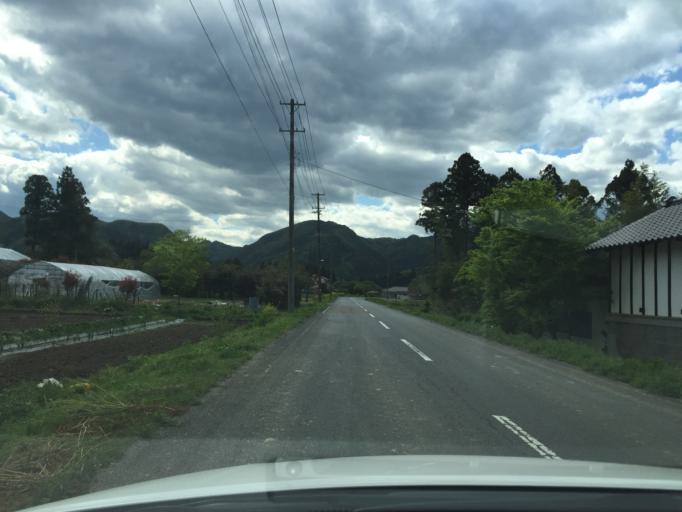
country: JP
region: Miyagi
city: Marumori
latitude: 37.7238
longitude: 140.8849
